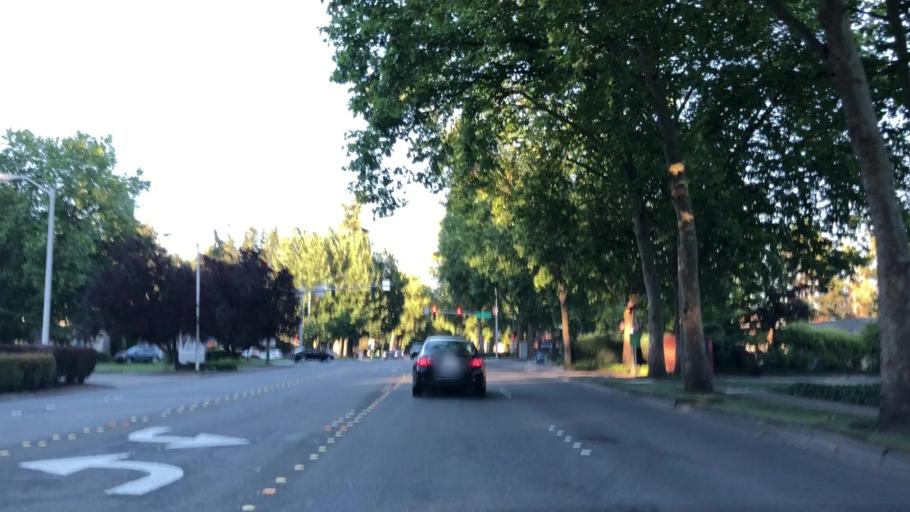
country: US
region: Washington
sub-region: King County
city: Redmond
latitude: 47.6724
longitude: -122.1145
